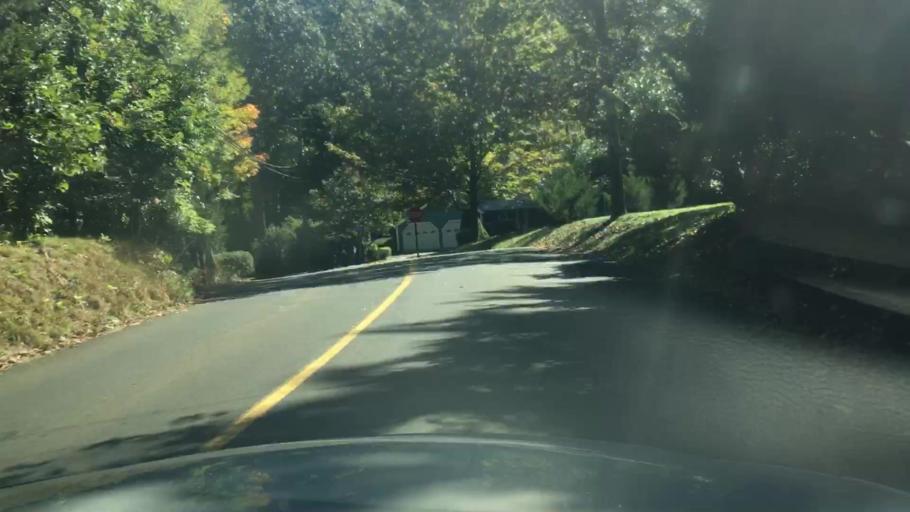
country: US
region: Connecticut
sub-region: Middlesex County
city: Essex Village
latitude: 41.3600
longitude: -72.4058
